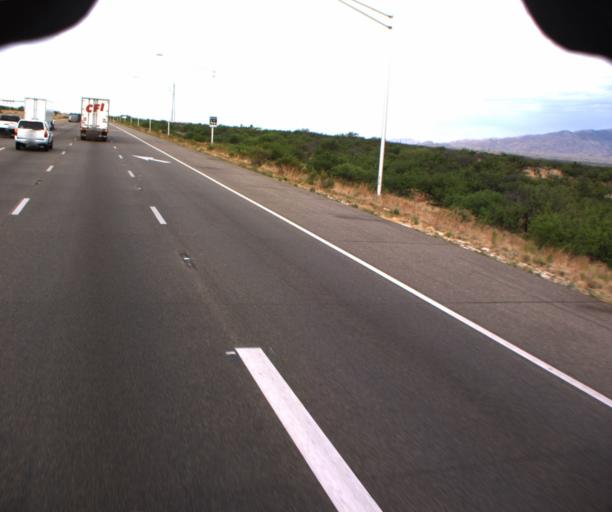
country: US
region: Arizona
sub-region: Cochise County
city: Whetstone
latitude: 31.9636
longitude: -110.3551
